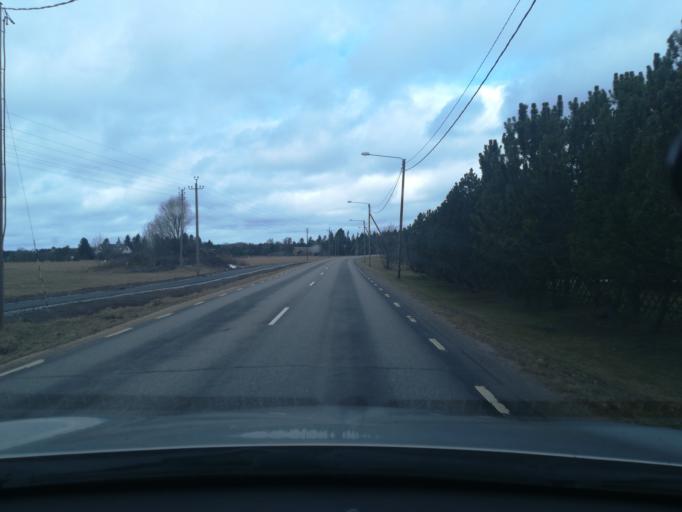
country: EE
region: Harju
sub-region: Harku vald
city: Tabasalu
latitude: 59.4307
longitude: 24.5216
